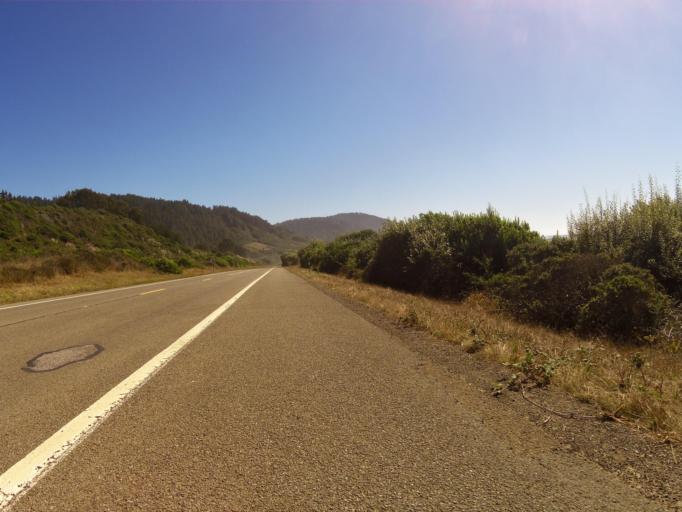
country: US
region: California
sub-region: Mendocino County
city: Fort Bragg
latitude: 39.6638
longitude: -123.7873
